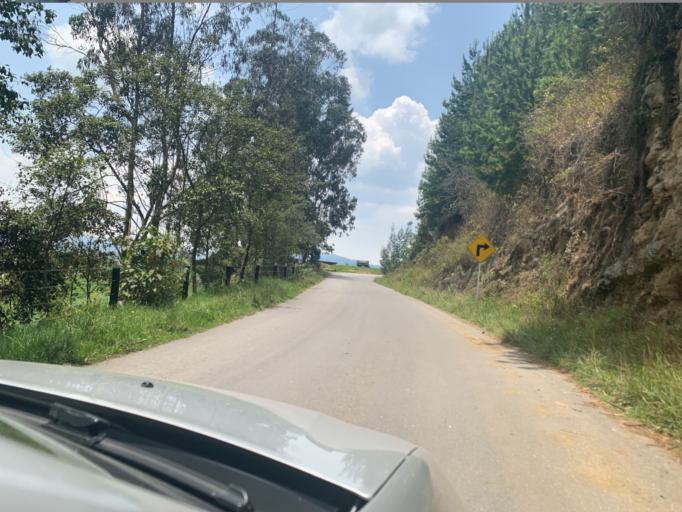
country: CO
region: Boyaca
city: Chiquinquira
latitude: 5.5456
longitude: -73.7513
